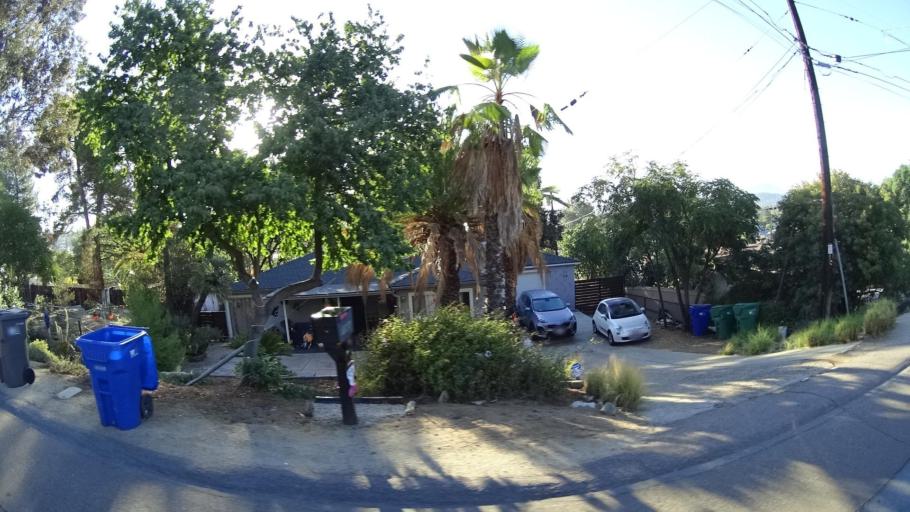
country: US
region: California
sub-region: San Diego County
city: Bostonia
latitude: 32.8153
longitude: -116.9415
